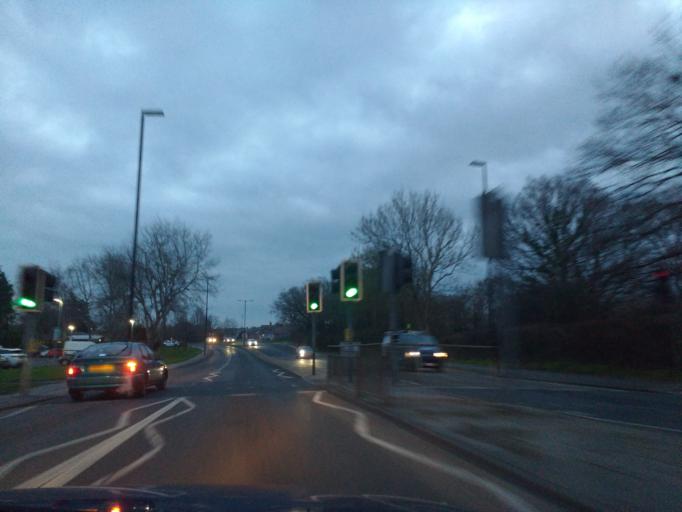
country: GB
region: England
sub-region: Isle of Wight
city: Newport
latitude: 50.7106
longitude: -1.3025
